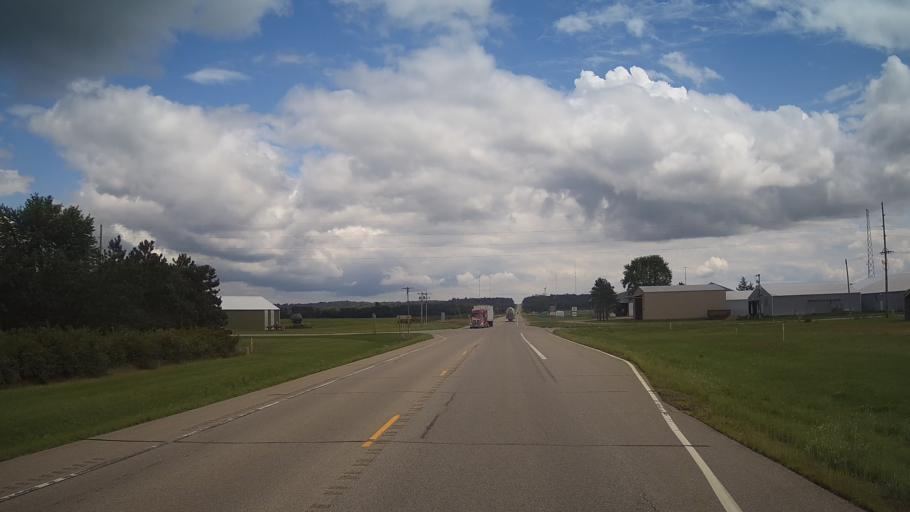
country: US
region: Wisconsin
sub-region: Marquette County
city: Westfield
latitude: 44.0221
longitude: -89.5997
